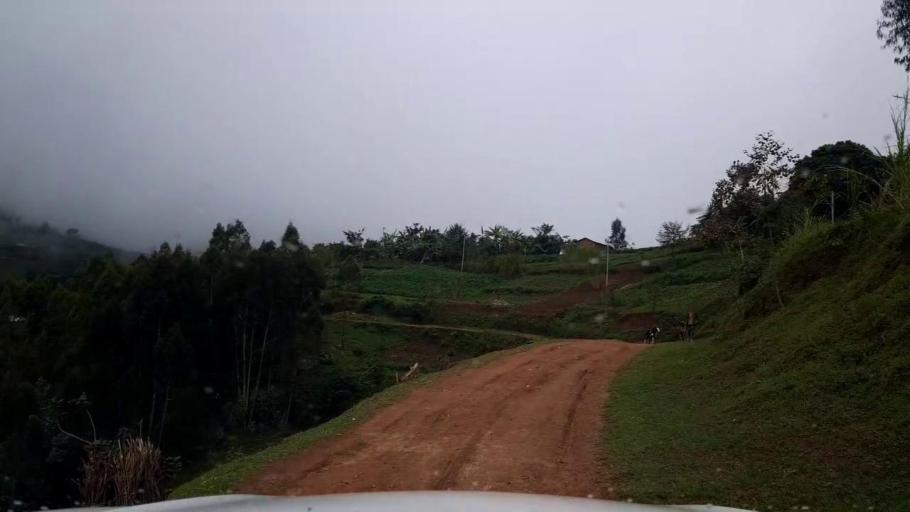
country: RW
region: Northern Province
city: Musanze
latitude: -1.5958
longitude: 29.7903
